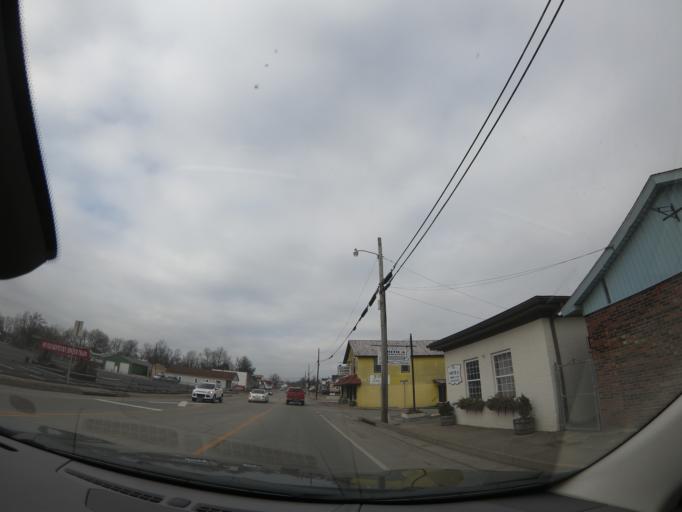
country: US
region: Kentucky
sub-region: Nelson County
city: Bardstown
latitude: 37.8176
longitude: -85.4641
